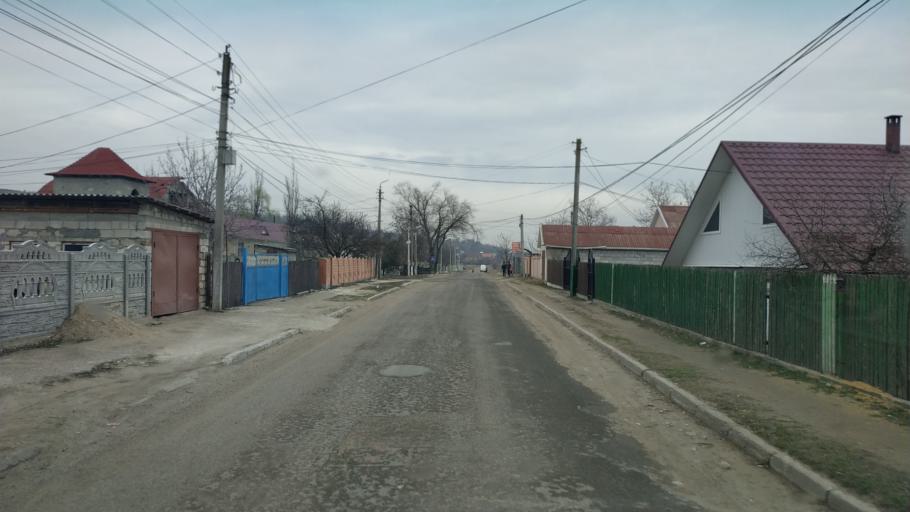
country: MD
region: Chisinau
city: Singera
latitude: 46.9335
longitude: 28.9992
